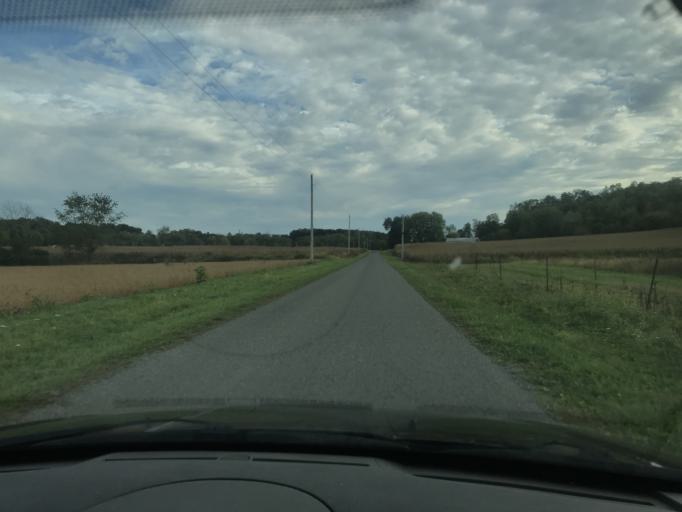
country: US
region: Ohio
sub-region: Logan County
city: West Liberty
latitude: 40.2519
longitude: -83.6959
